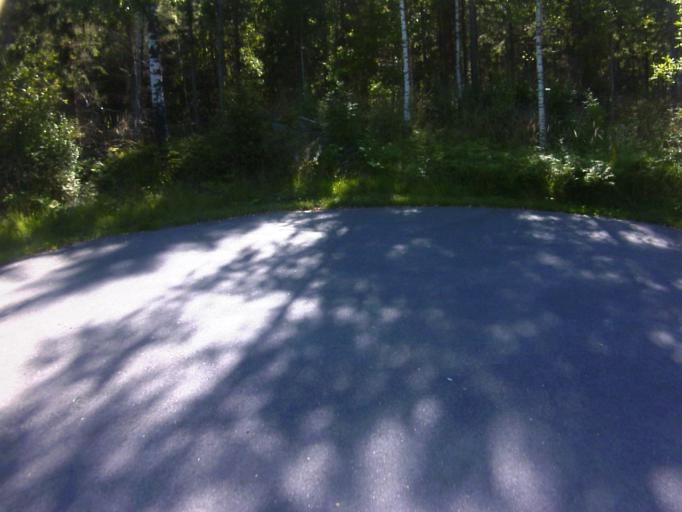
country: SE
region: Soedermanland
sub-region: Eskilstuna Kommun
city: Hallbybrunn
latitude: 59.3411
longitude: 16.4107
